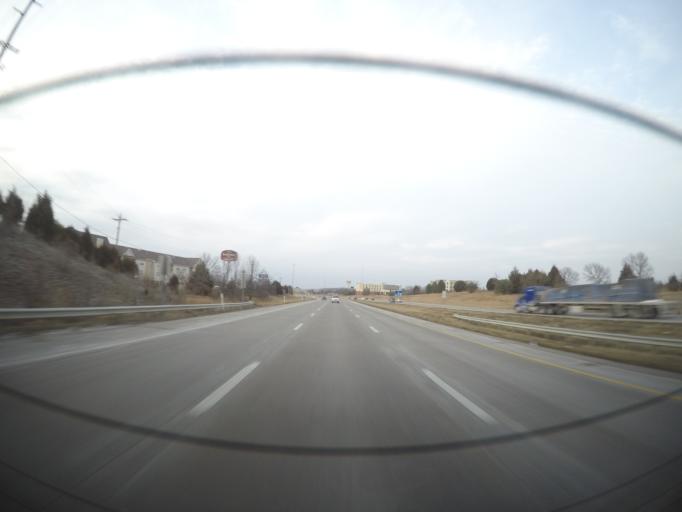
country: US
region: Kansas
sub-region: Shawnee County
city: Topeka
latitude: 39.0366
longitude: -95.7571
